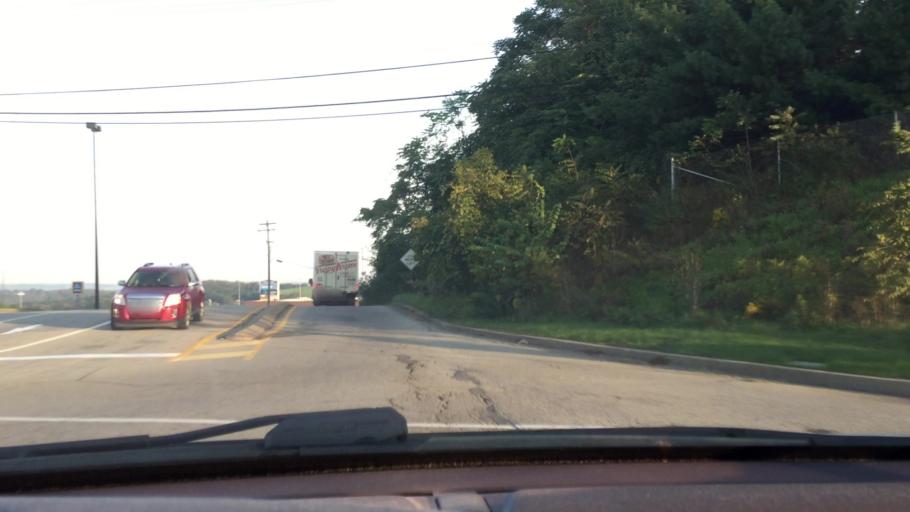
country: US
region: Pennsylvania
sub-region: Washington County
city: East Washington
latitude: 40.1806
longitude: -80.2226
